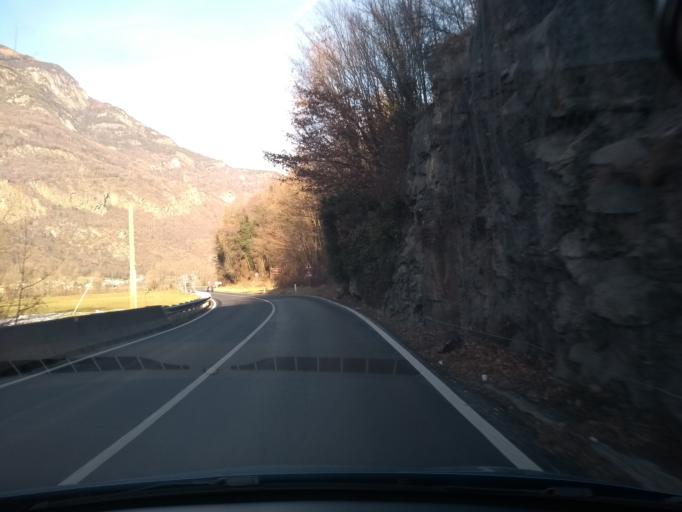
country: IT
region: Aosta Valley
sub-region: Valle d'Aosta
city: Champdepraz
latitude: 45.6867
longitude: 7.6723
